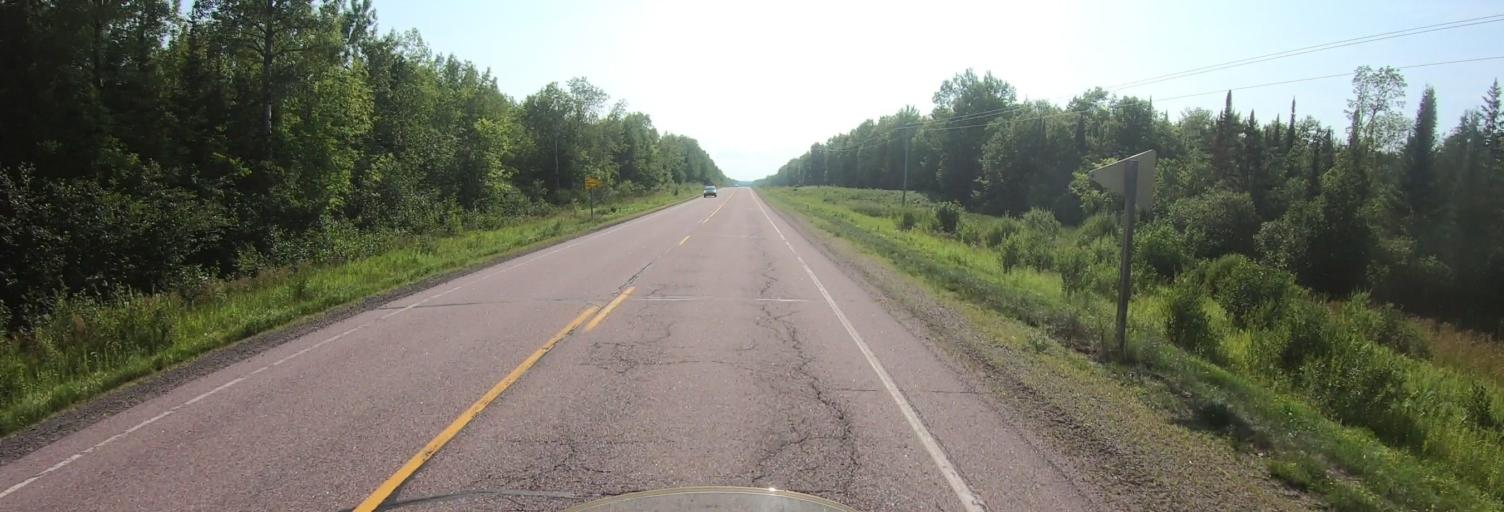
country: US
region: Wisconsin
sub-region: Iron County
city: Hurley
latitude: 46.3616
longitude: -90.4466
